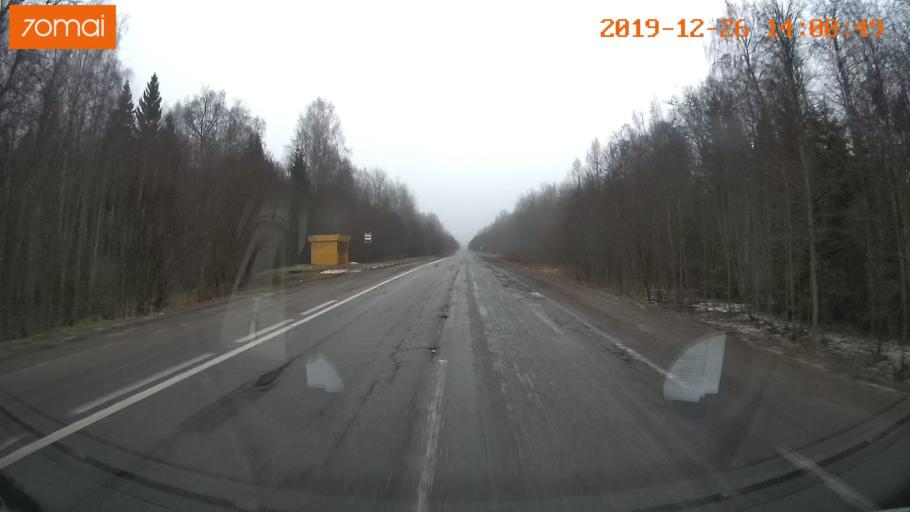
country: RU
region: Jaroslavl
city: Poshekhon'ye
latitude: 58.5553
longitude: 38.7510
